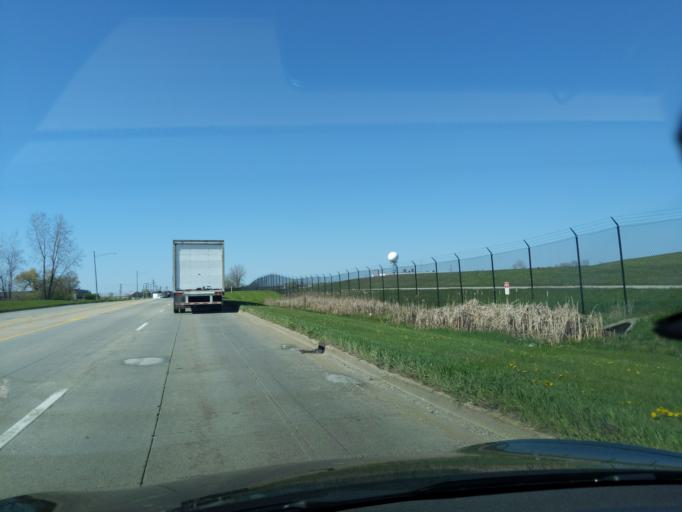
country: US
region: Michigan
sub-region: Kent County
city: East Grand Rapids
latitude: 42.8886
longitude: -85.5473
